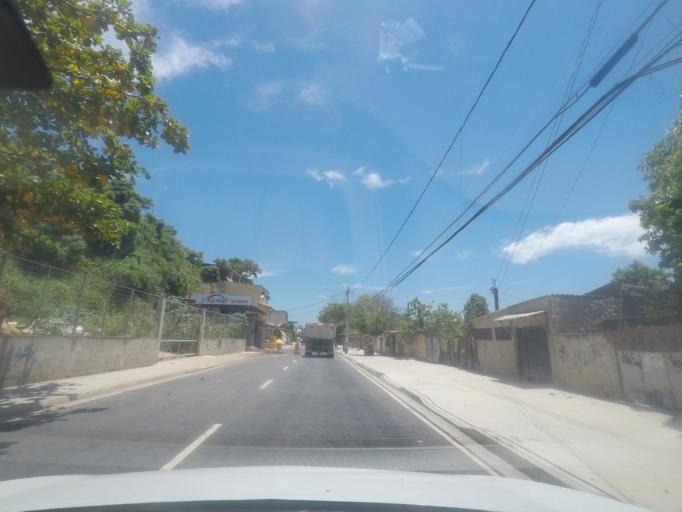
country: BR
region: Rio de Janeiro
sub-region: Itaguai
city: Itaguai
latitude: -22.9243
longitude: -43.6911
